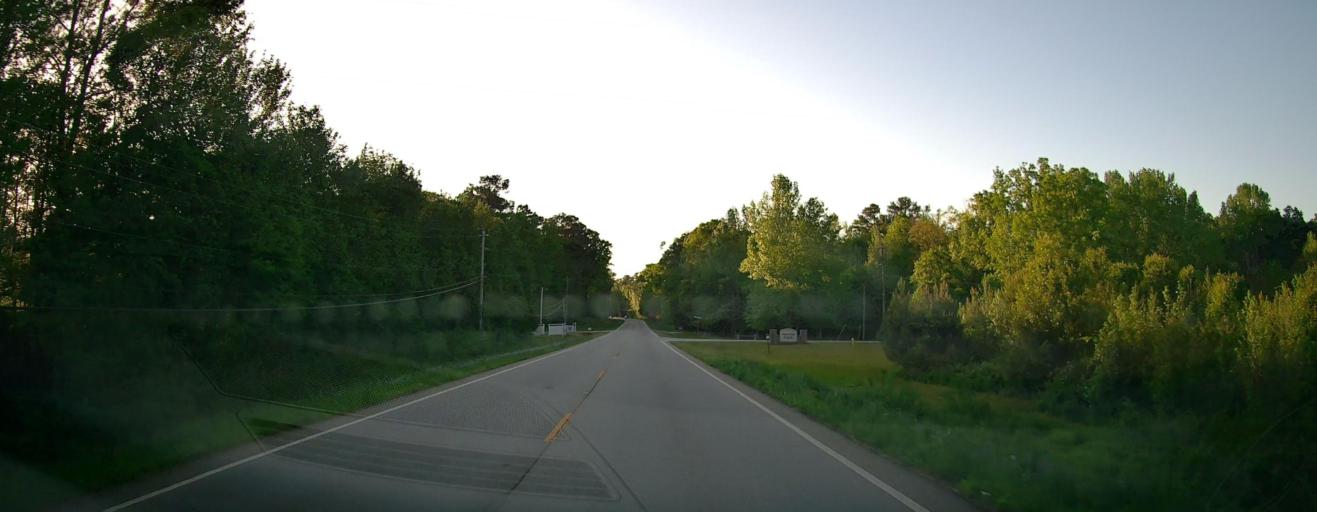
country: US
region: Georgia
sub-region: Newton County
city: Covington
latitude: 33.5836
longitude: -83.7822
